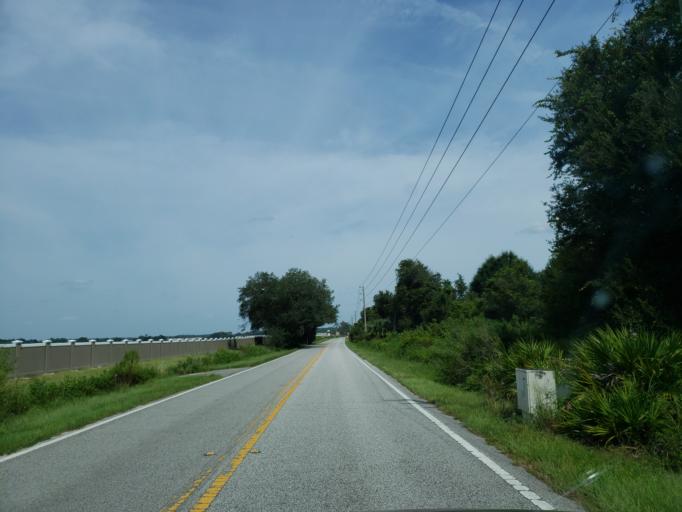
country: US
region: Florida
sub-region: Pasco County
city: Wesley Chapel
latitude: 28.2807
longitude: -82.2946
